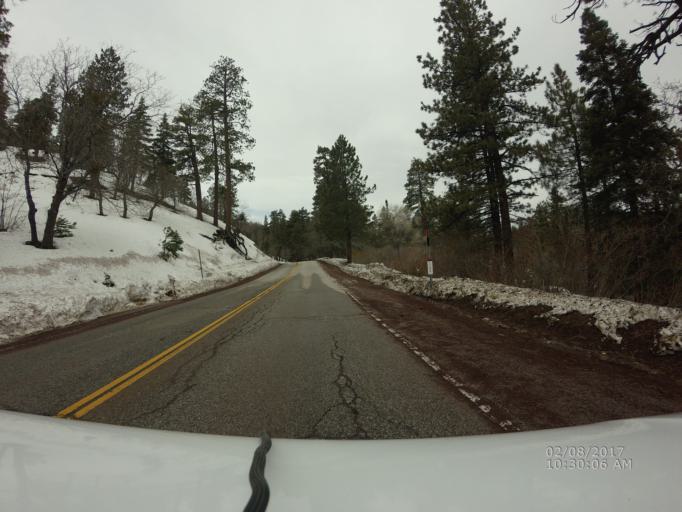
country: US
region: California
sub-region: San Bernardino County
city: Pinon Hills
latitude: 34.3900
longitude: -117.7191
